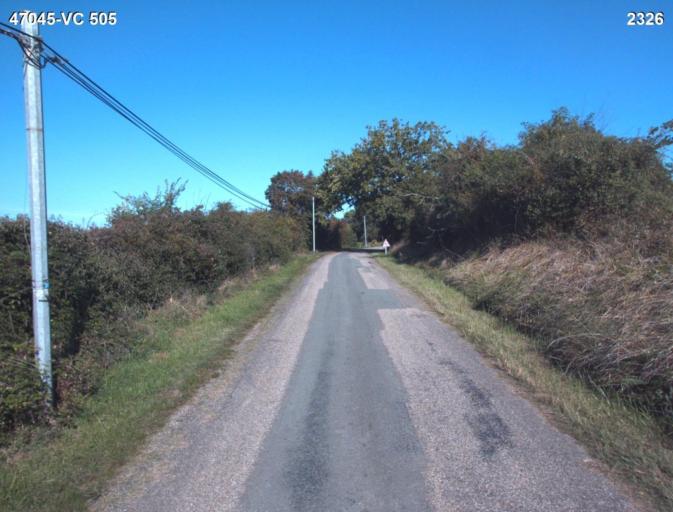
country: FR
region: Aquitaine
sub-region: Departement du Lot-et-Garonne
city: Nerac
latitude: 44.1440
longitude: 0.4153
